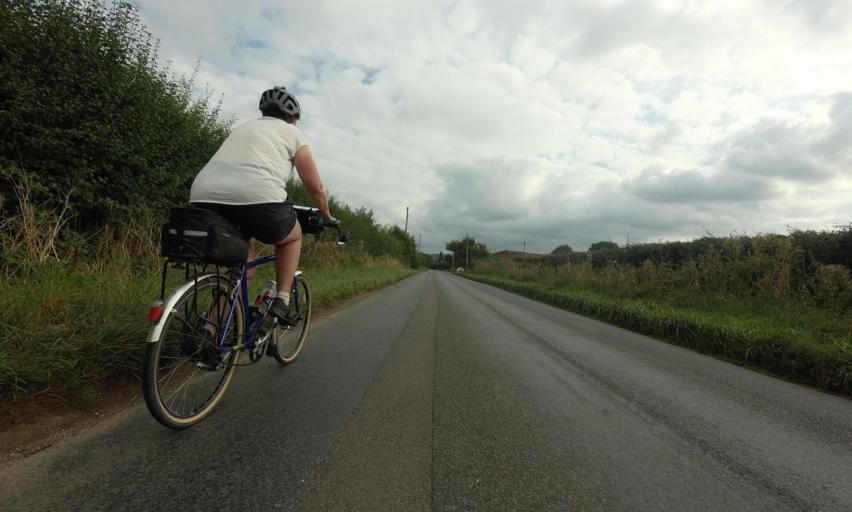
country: GB
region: England
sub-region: Gloucestershire
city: Winchcombe
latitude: 51.9901
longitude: -2.0013
